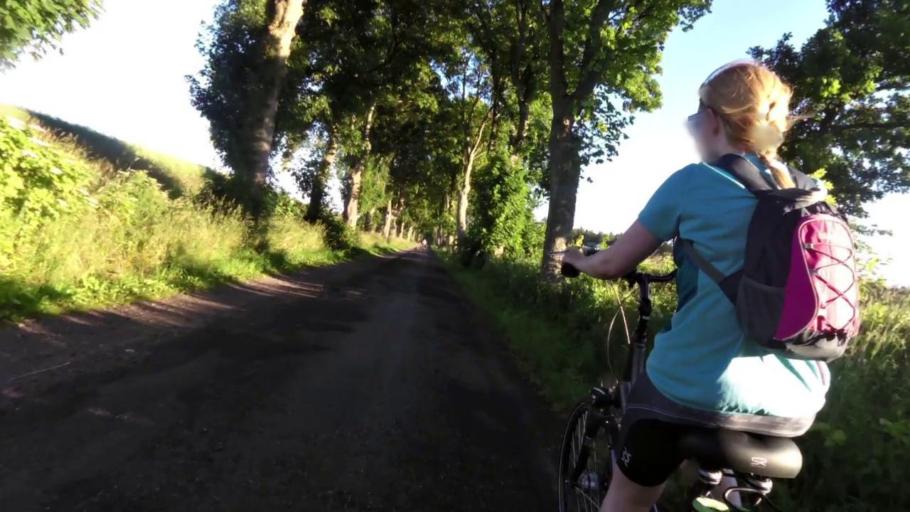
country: PL
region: West Pomeranian Voivodeship
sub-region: Koszalin
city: Koszalin
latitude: 54.0700
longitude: 16.1252
